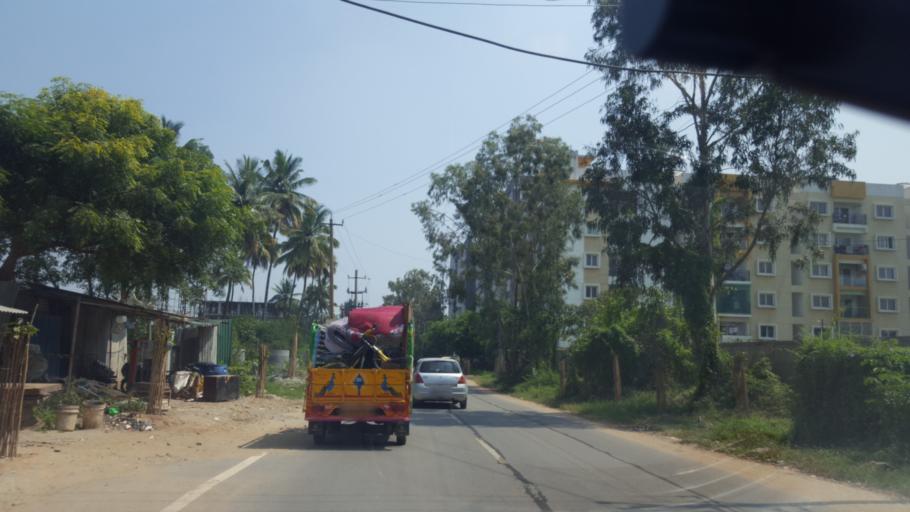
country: IN
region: Karnataka
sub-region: Bangalore Urban
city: Bangalore
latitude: 12.9381
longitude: 77.7118
